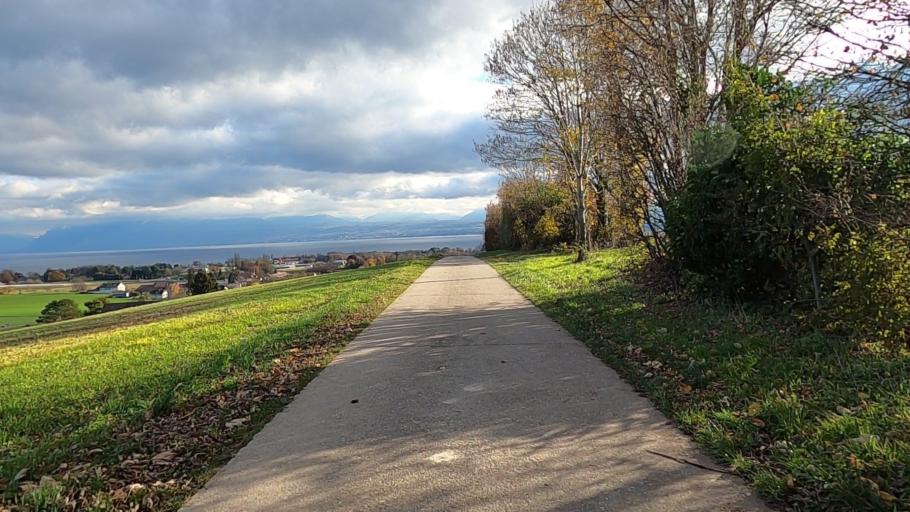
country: CH
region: Vaud
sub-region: Morges District
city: Saint-Prex
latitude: 46.5098
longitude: 6.4581
